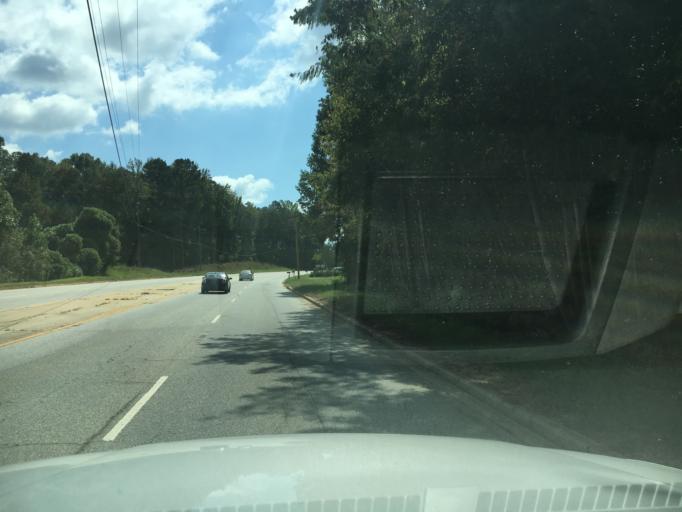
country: US
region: South Carolina
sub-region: Greenwood County
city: Ware Shoals
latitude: 34.3580
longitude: -82.2187
